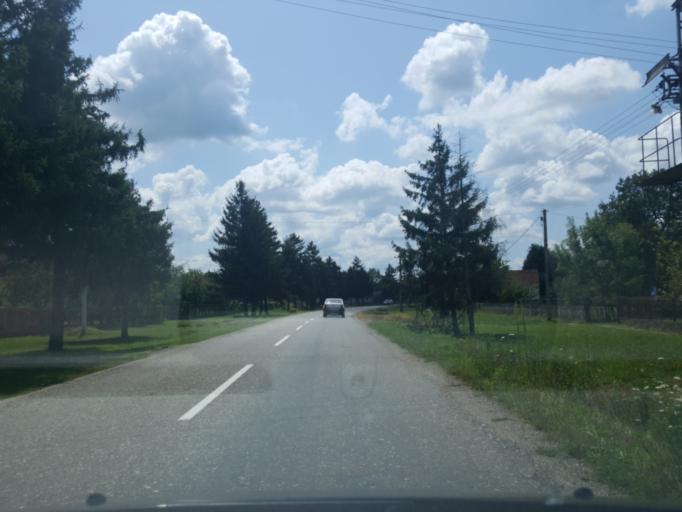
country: RS
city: Zminjak
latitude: 44.7418
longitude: 19.4674
